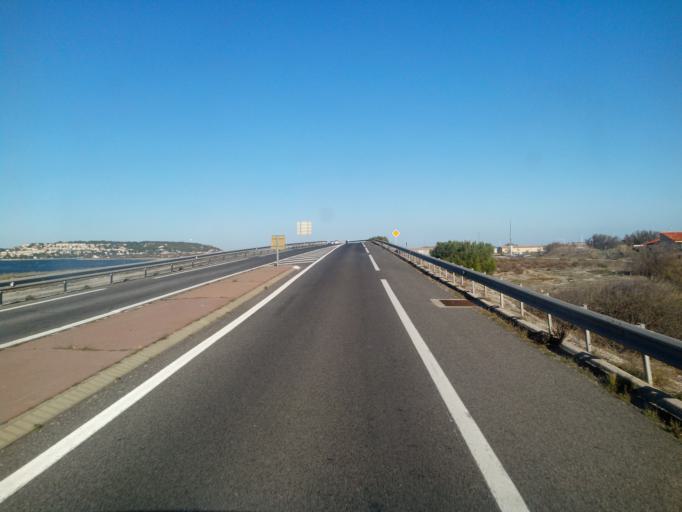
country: FR
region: Languedoc-Roussillon
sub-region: Departement de l'Aude
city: Leucate
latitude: 42.8840
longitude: 3.0463
